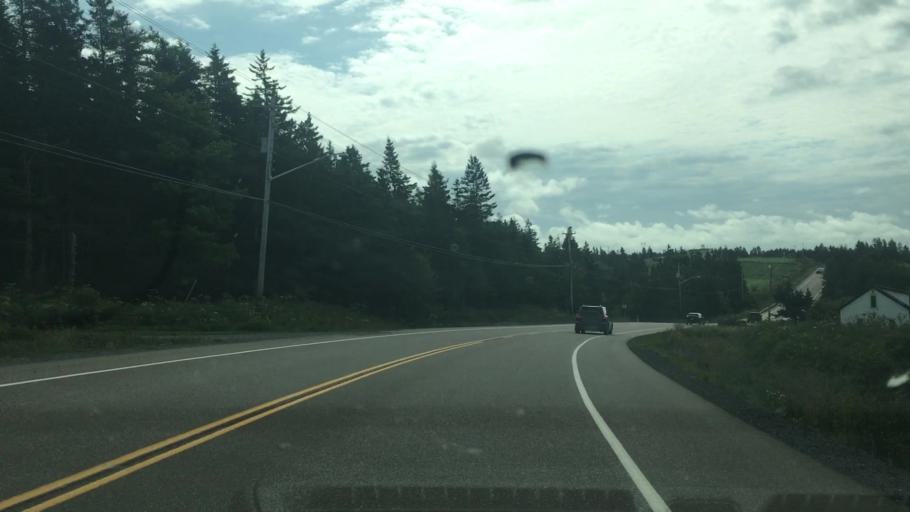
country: CA
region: Nova Scotia
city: Princeville
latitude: 45.7017
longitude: -60.7377
